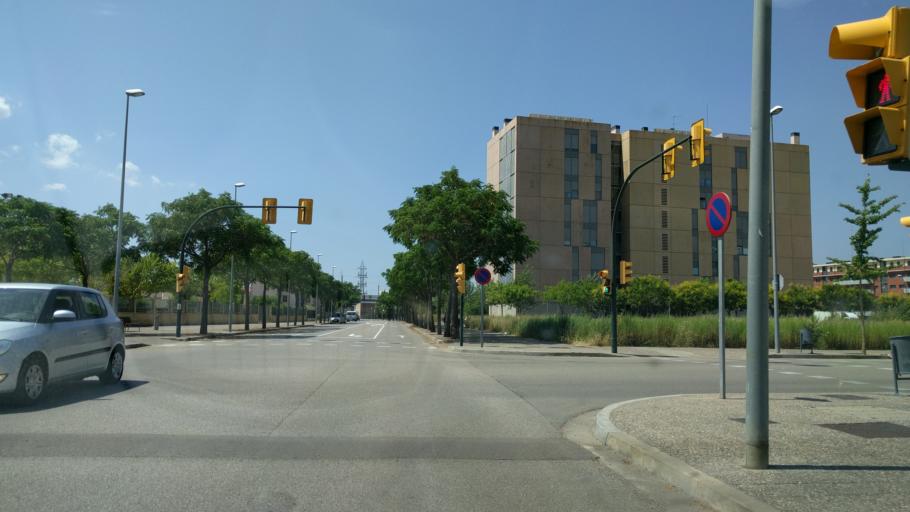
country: ES
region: Catalonia
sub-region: Provincia de Girona
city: Salt
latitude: 41.9717
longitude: 2.8035
